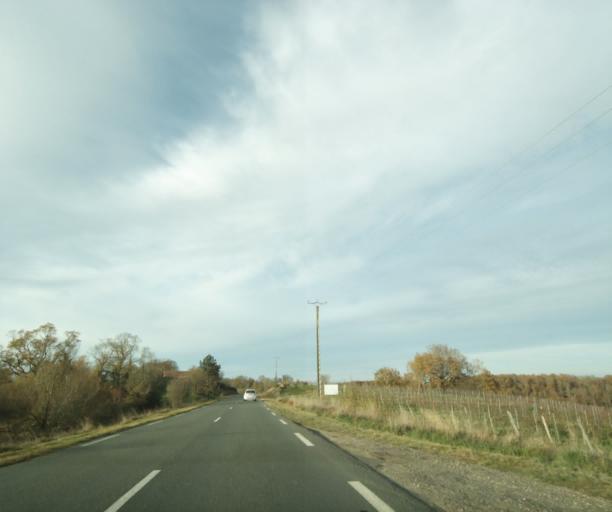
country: FR
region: Midi-Pyrenees
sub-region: Departement du Gers
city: Eauze
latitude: 43.7948
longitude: 0.0999
